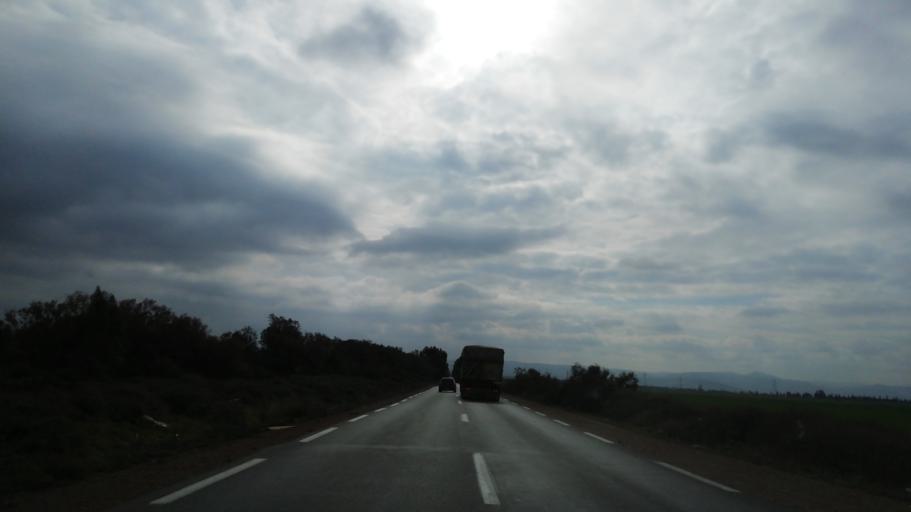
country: DZ
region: Oran
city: Sidi ech Chahmi
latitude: 35.5861
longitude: -0.4533
